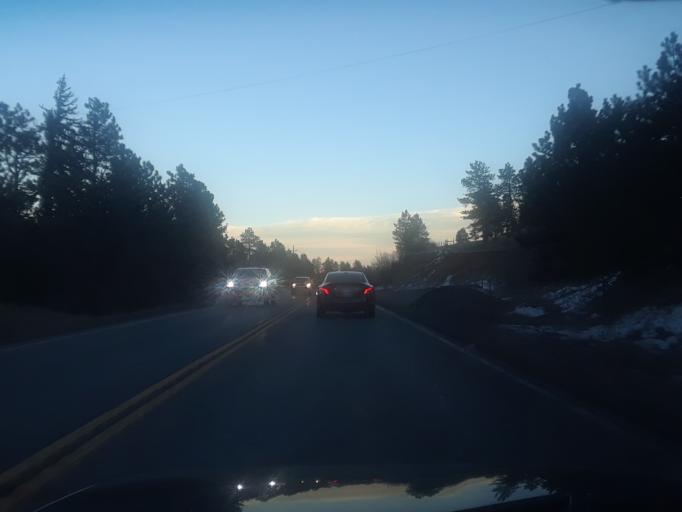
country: US
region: Colorado
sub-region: Clear Creek County
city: Georgetown
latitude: 39.4332
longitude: -105.5829
